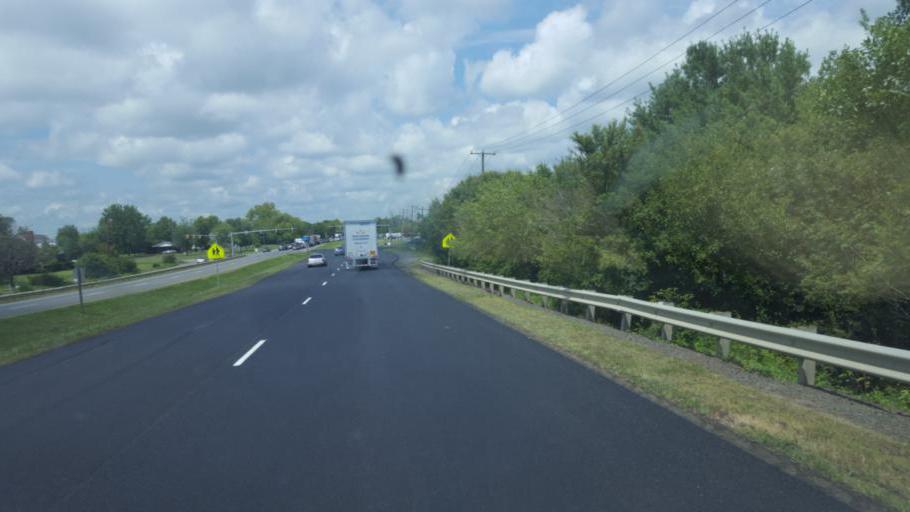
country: US
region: Virginia
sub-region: Fauquier County
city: Bealeton
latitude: 38.5747
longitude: -77.7639
